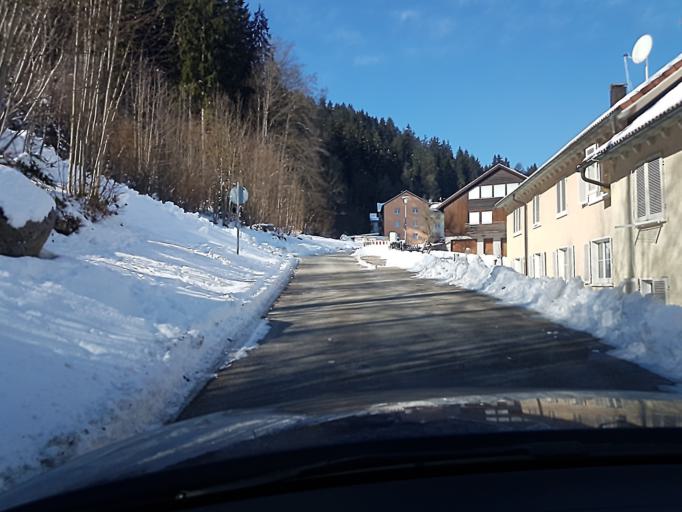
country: DE
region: Baden-Wuerttemberg
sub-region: Freiburg Region
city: Triberg im Schwarzwald
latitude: 48.1326
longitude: 8.2194
